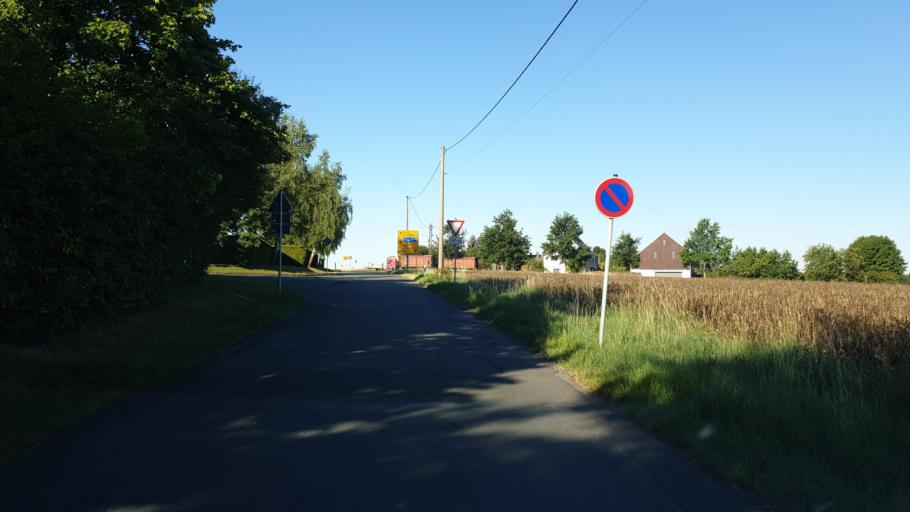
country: DE
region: Saxony
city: Hirschfeld
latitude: 50.6458
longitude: 12.4213
